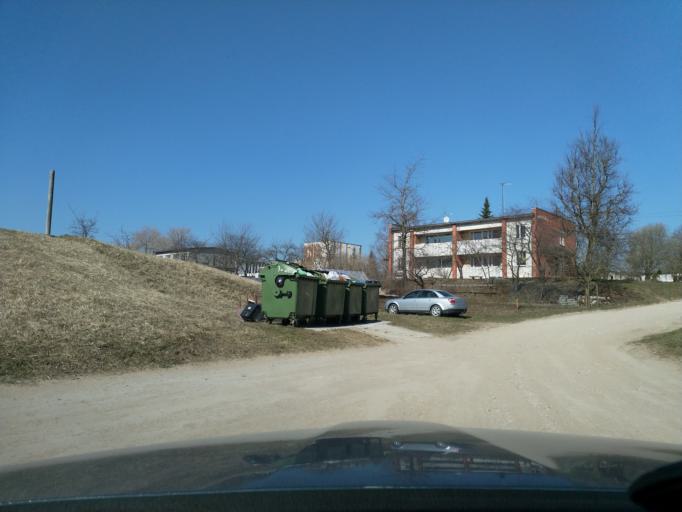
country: LV
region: Kuldigas Rajons
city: Kuldiga
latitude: 56.9644
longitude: 21.9254
